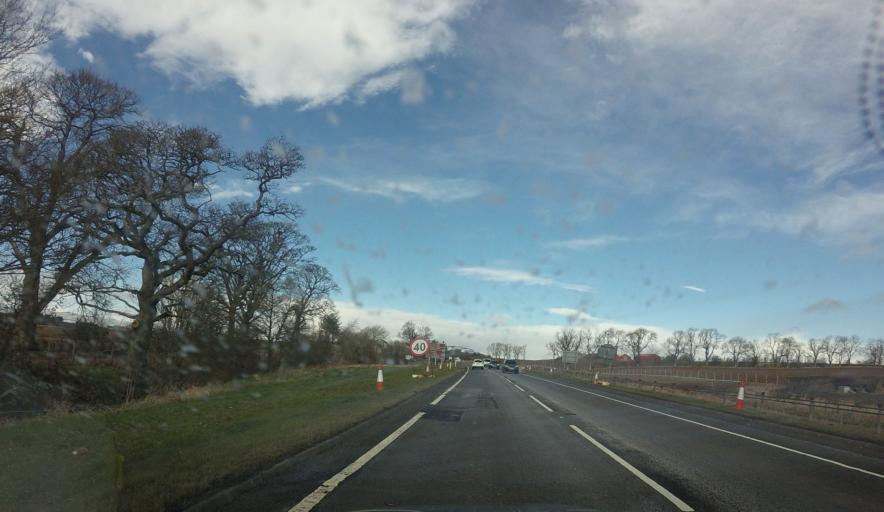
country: GB
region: Scotland
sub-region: Perth and Kinross
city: Bankfoot
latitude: 56.4784
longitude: -3.4914
